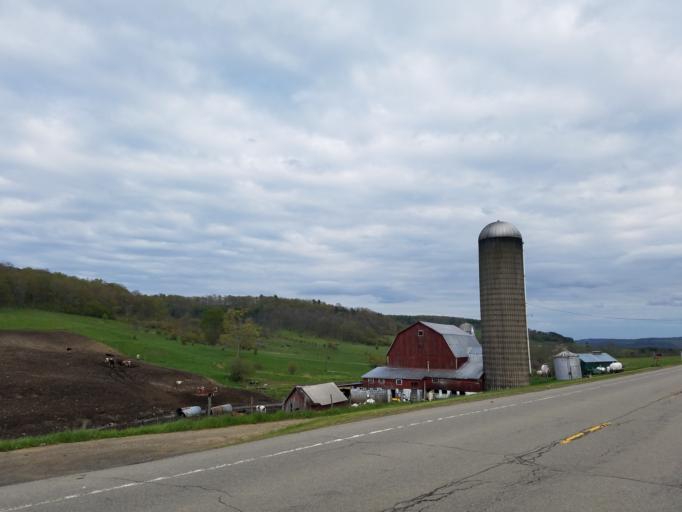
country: US
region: New York
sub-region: Steuben County
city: Canisteo
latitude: 42.1520
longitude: -77.5192
